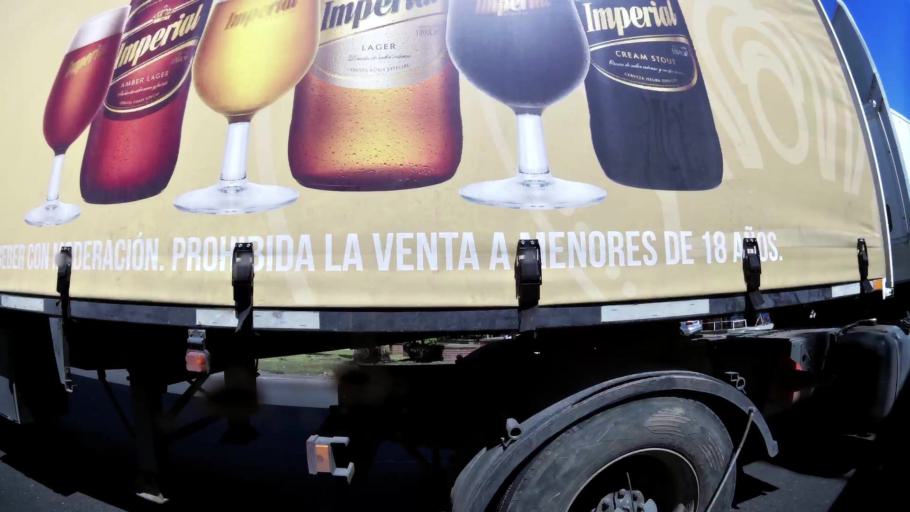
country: AR
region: Buenos Aires
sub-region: Partido de Quilmes
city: Quilmes
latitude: -34.7165
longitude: -58.3048
